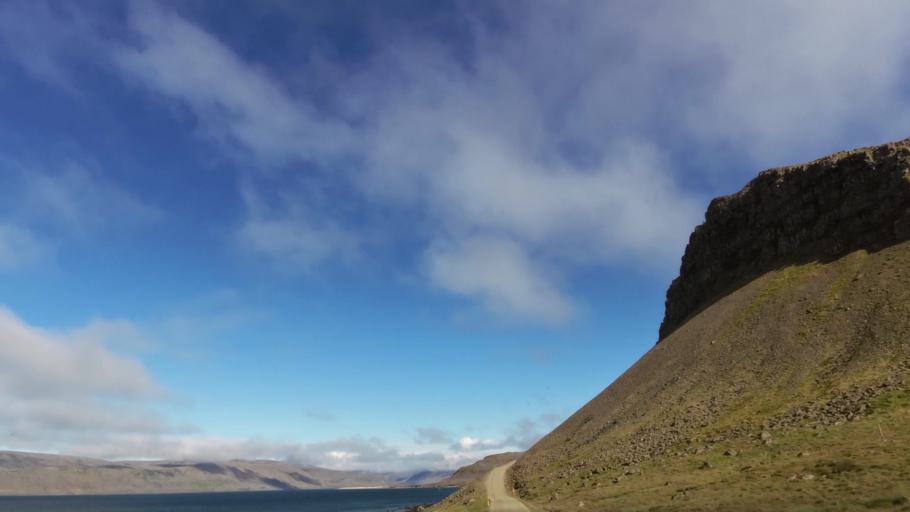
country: IS
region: West
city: Olafsvik
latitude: 65.5686
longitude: -24.0532
